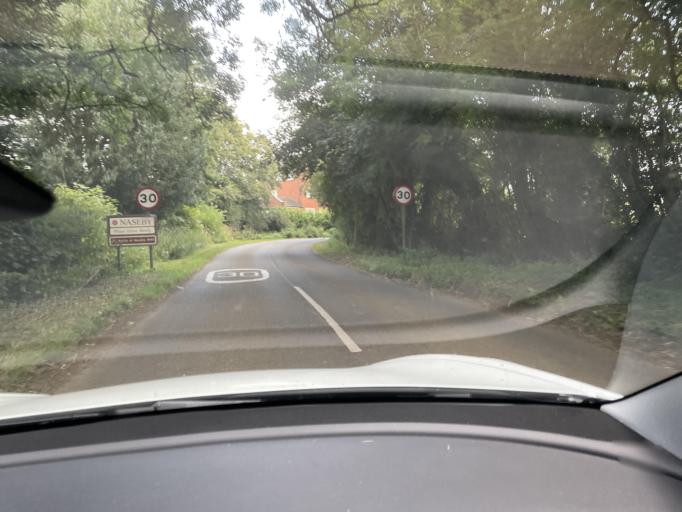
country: GB
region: England
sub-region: Leicestershire
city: Market Harborough
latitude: 52.3992
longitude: -0.9911
